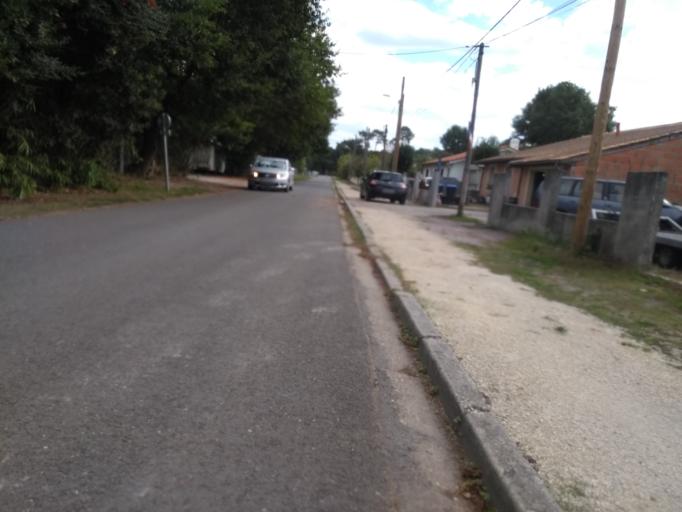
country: FR
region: Aquitaine
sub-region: Departement de la Gironde
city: Saint-Aubin-de-Medoc
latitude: 44.7723
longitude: -0.6981
